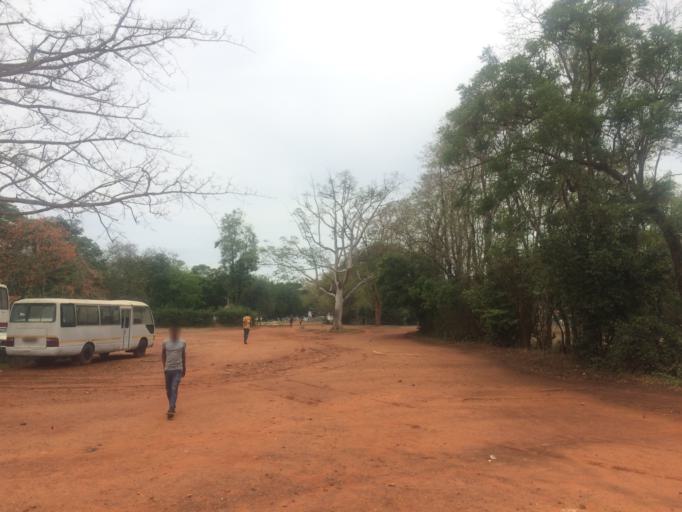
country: GH
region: Greater Accra
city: Medina Estates
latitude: 5.6488
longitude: -0.1817
